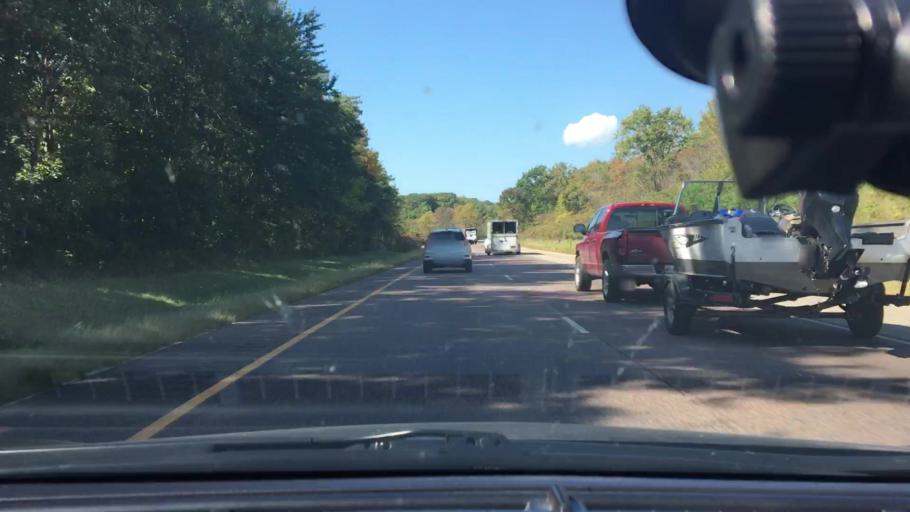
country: US
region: Wisconsin
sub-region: Dunn County
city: Boyceville
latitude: 44.9190
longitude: -92.0619
